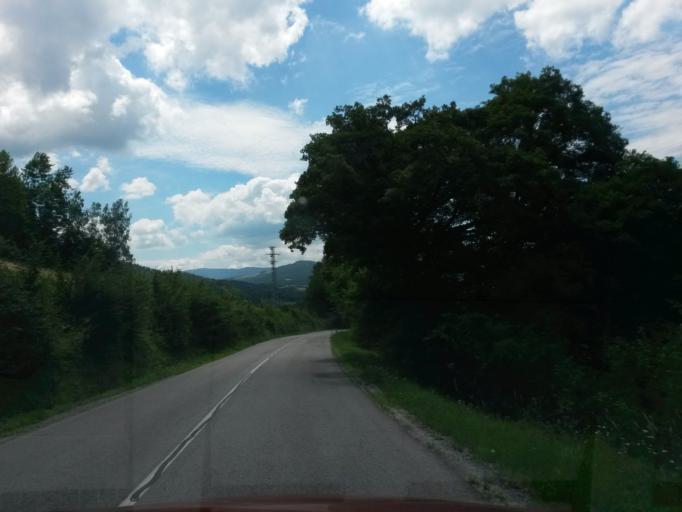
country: SK
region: Kosicky
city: Gelnica
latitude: 48.8979
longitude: 21.0200
